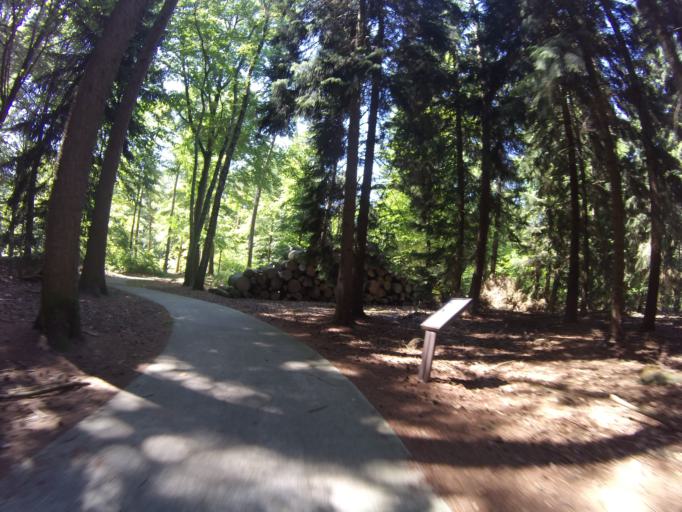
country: NL
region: Drenthe
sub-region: Gemeente Emmen
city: Emmen
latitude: 52.7887
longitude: 6.9201
